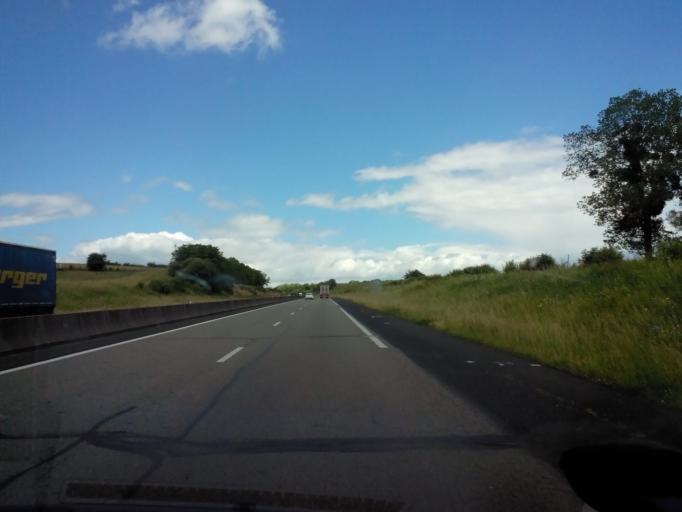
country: FR
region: Lorraine
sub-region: Departement des Vosges
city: Lamarche
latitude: 48.1037
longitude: 5.6490
